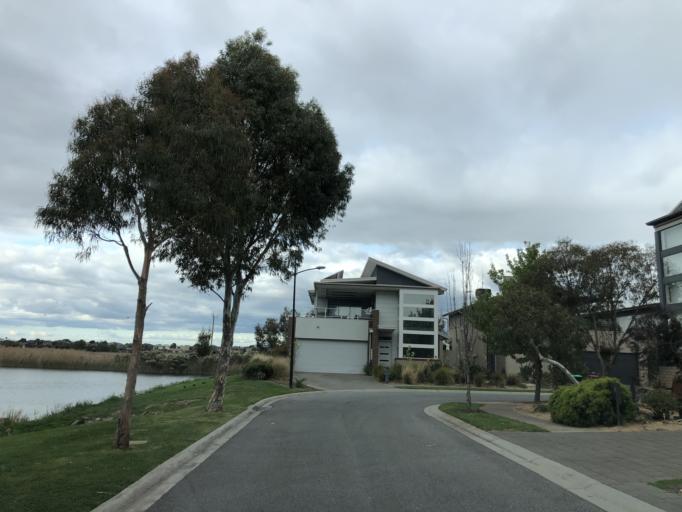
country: AU
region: Victoria
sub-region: Kingston
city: Patterson Lakes
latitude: -38.0644
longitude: 145.1377
